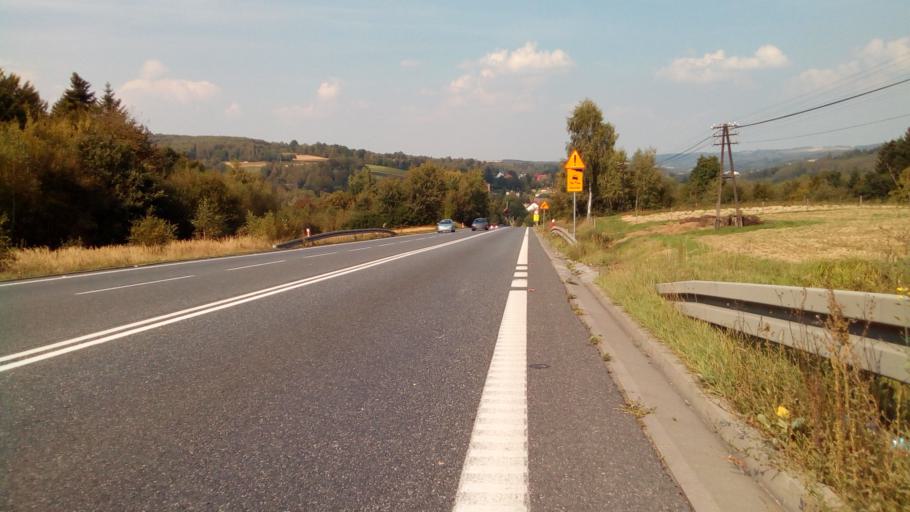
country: PL
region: Subcarpathian Voivodeship
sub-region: Powiat strzyzowski
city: Jawornik
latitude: 49.8387
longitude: 21.8887
